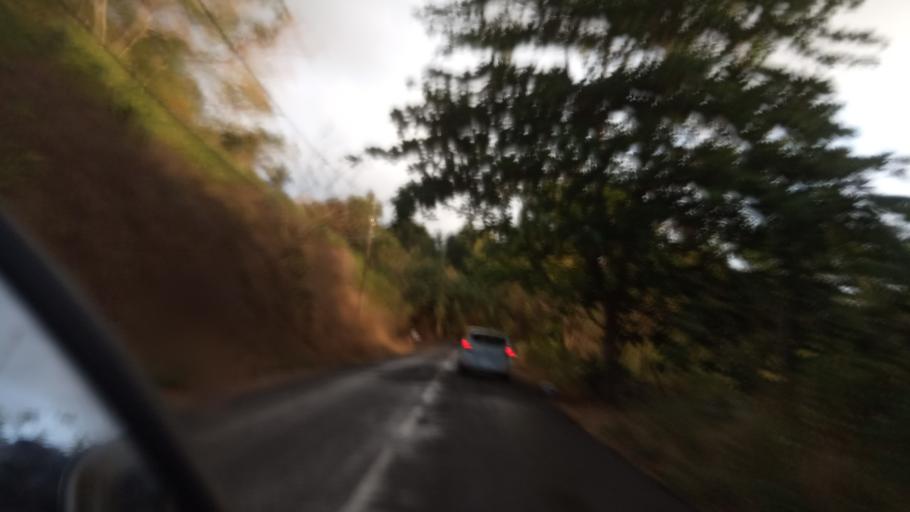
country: YT
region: Kani-Keli
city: Kani Keli
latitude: -12.9322
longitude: 45.1045
